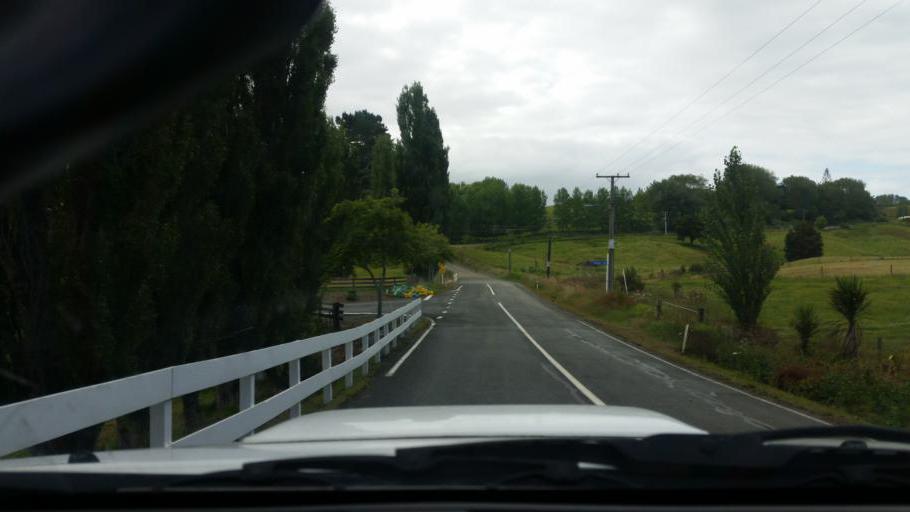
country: NZ
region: Auckland
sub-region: Auckland
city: Wellsford
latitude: -36.1315
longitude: 174.3591
